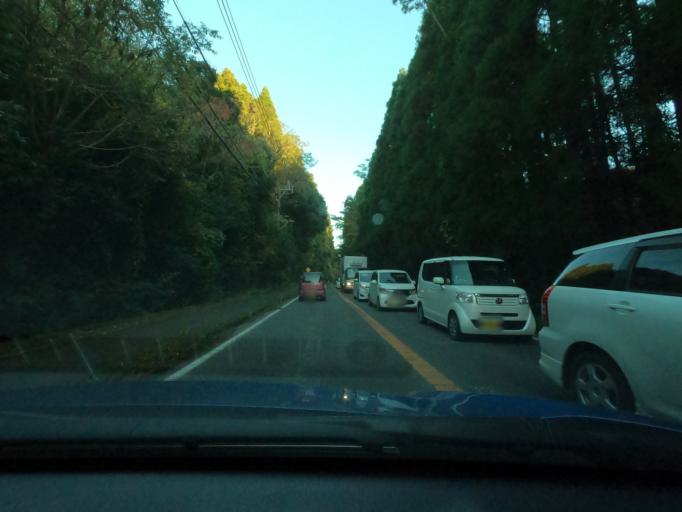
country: JP
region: Kagoshima
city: Satsumasendai
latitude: 31.8136
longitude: 130.3760
